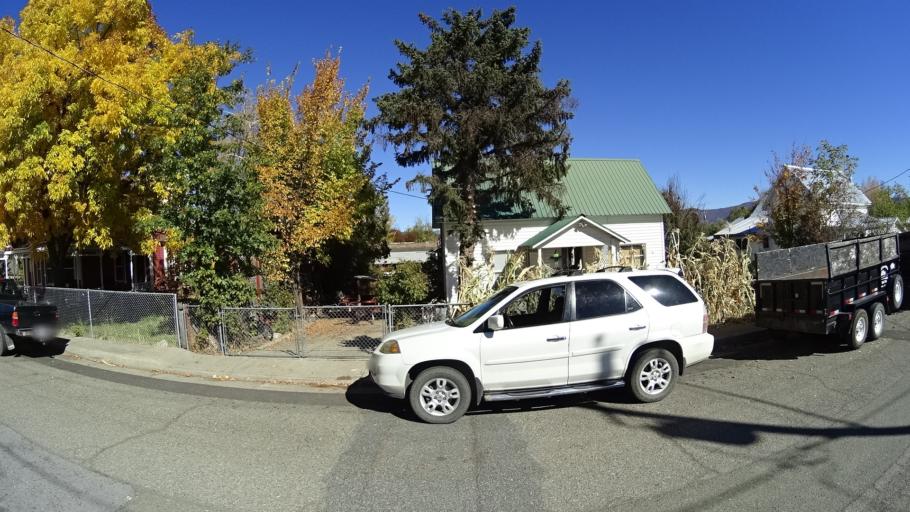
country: US
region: California
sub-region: Siskiyou County
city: Yreka
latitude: 41.4562
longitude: -122.8982
